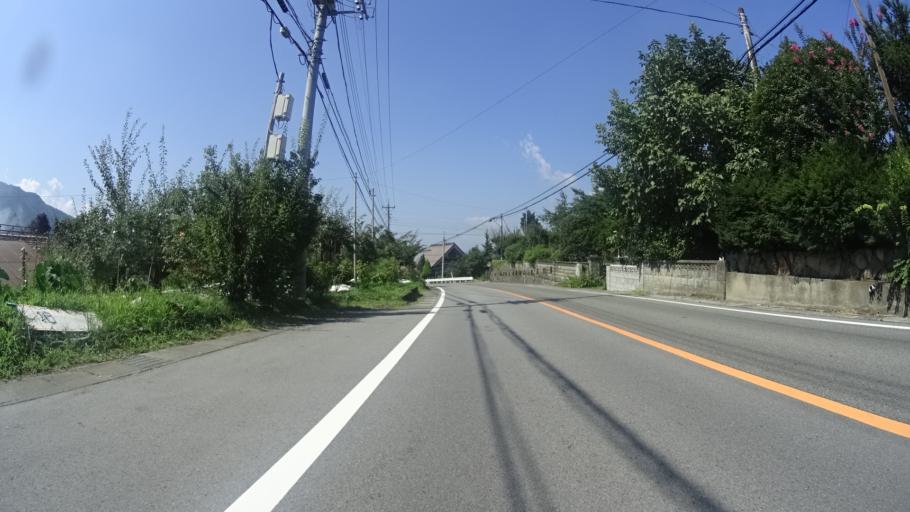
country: JP
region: Yamanashi
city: Enzan
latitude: 35.7259
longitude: 138.7568
